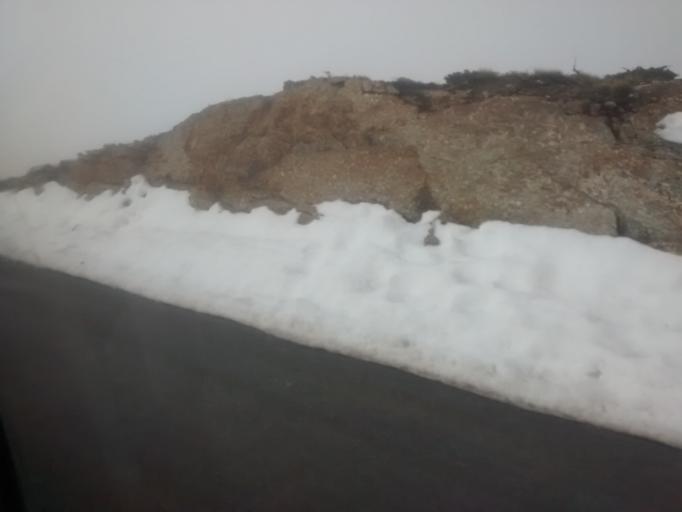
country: PT
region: Guarda
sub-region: Seia
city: Seia
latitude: 40.3594
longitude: -7.6544
